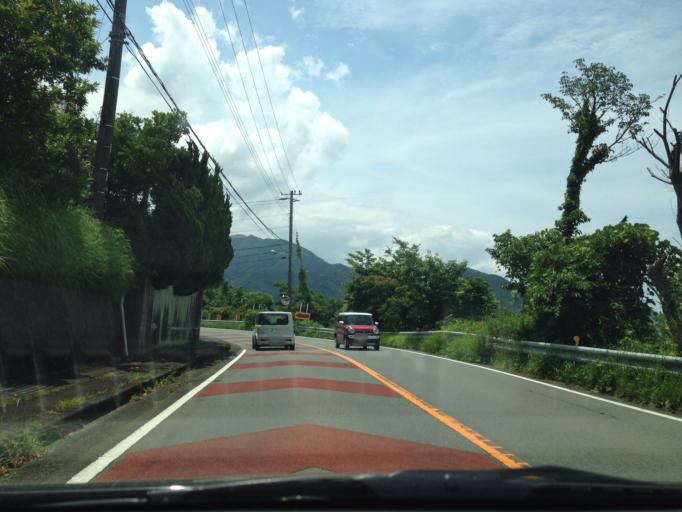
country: JP
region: Shizuoka
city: Heda
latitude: 34.8658
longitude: 138.7626
